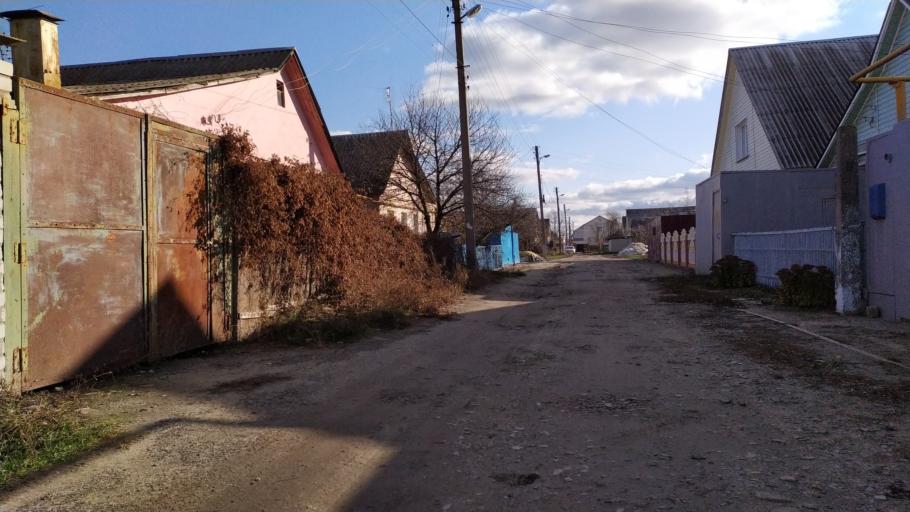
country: RU
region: Kursk
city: Kursk
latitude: 51.6466
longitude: 36.1545
